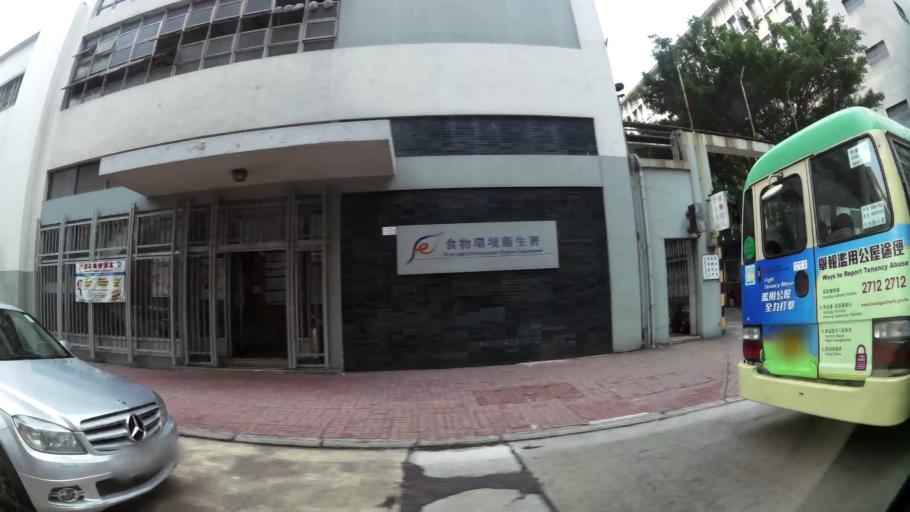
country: HK
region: Kowloon City
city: Kowloon
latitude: 22.3208
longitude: 114.1714
